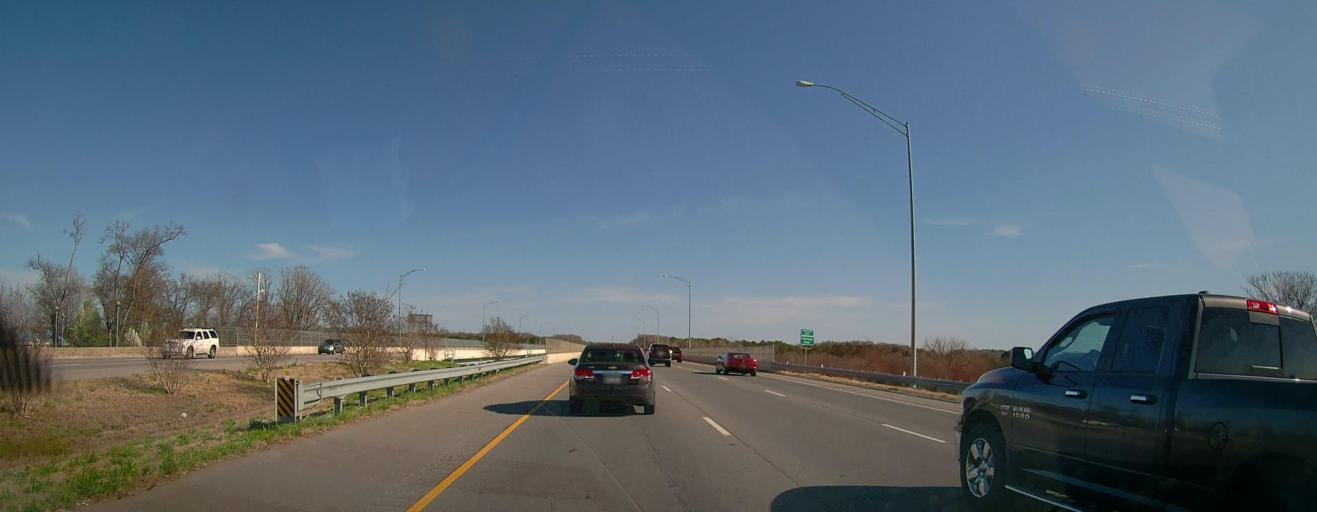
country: US
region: Alabama
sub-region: Lauderdale County
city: East Florence
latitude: 34.8011
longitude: -87.6510
